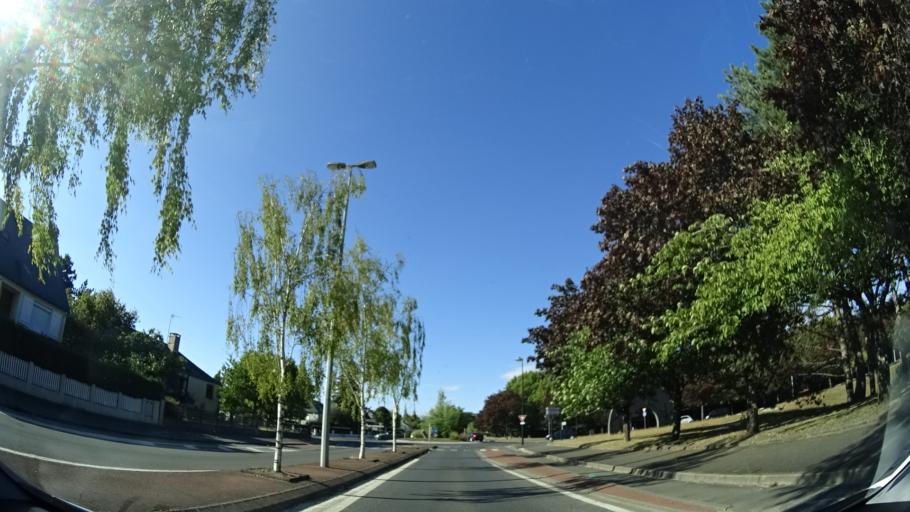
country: FR
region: Centre
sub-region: Departement du Loiret
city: Saint-Jean-de-Braye
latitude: 47.9140
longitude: 1.9781
